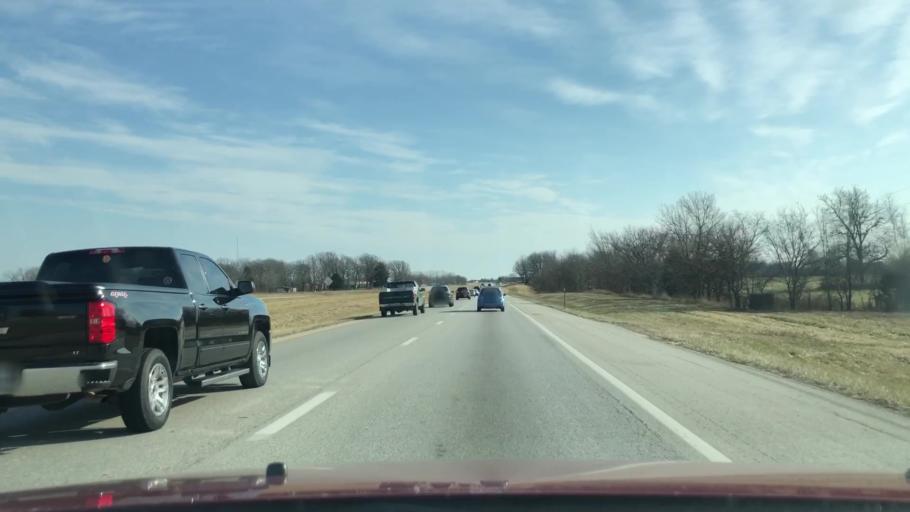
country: US
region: Missouri
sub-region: Webster County
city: Rogersville
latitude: 37.1186
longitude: -93.1154
